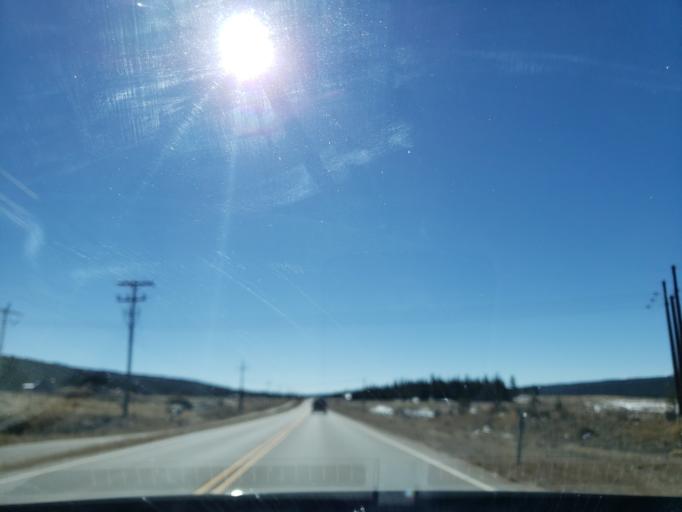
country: US
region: Colorado
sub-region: Park County
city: Fairplay
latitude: 39.2686
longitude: -106.0462
